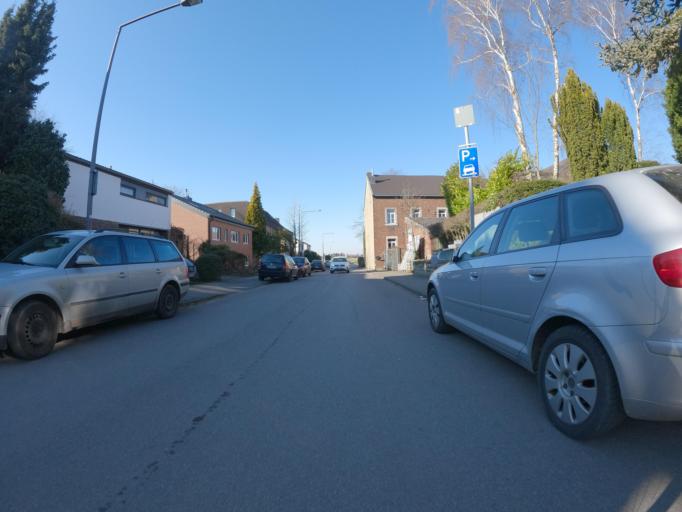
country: DE
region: North Rhine-Westphalia
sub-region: Regierungsbezirk Koln
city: Aachen
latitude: 50.8163
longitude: 6.0551
